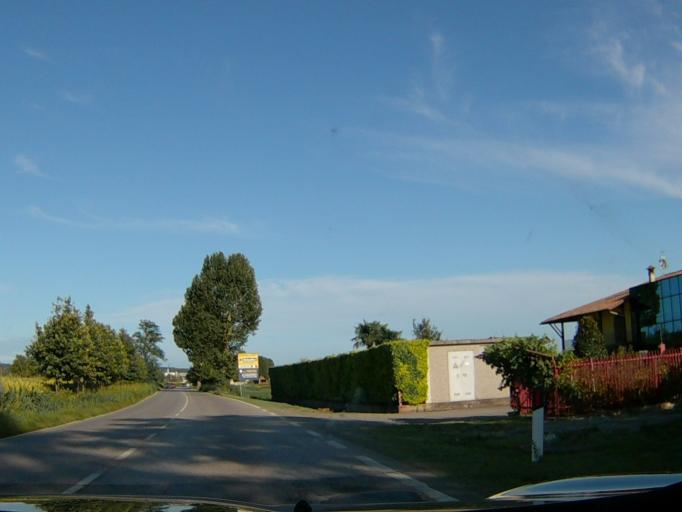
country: IT
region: Lombardy
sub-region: Provincia di Brescia
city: Ponte San Marco
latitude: 45.4700
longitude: 10.4434
